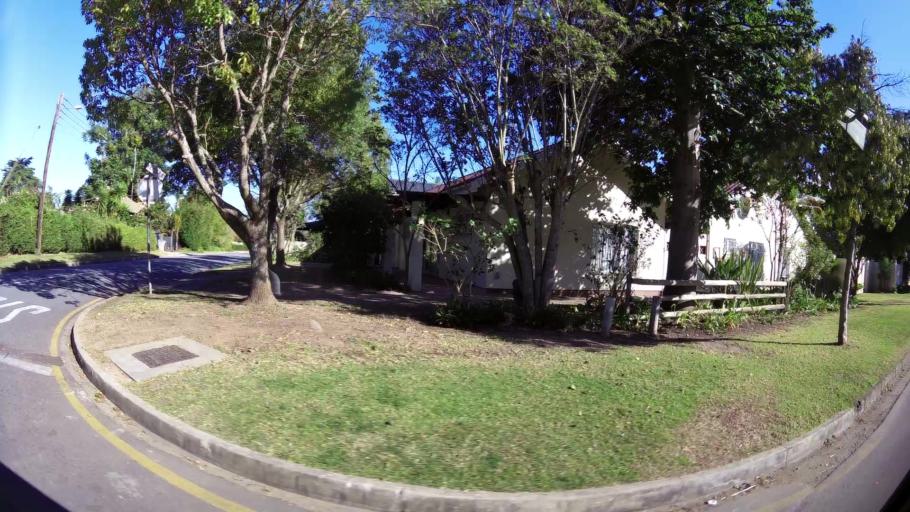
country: ZA
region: Western Cape
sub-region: Eden District Municipality
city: George
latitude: -33.9552
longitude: 22.4239
